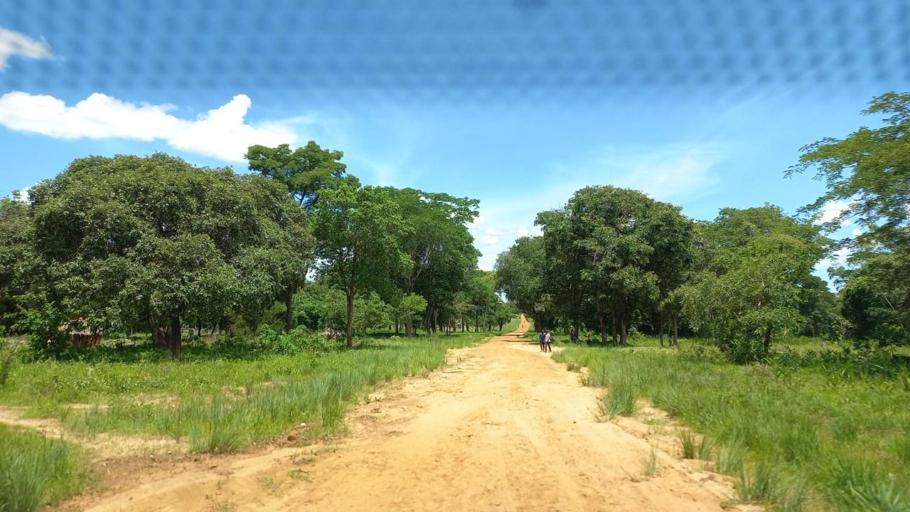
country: ZM
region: North-Western
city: Kabompo
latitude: -12.7521
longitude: 24.2686
